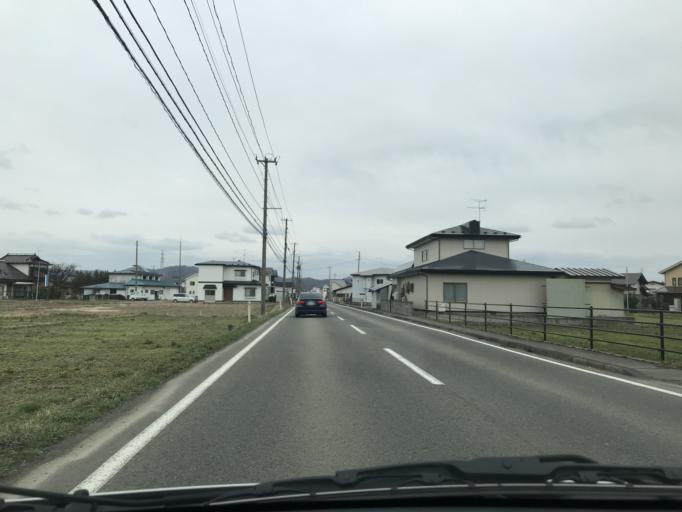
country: JP
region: Iwate
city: Kitakami
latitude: 39.2752
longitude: 141.0897
